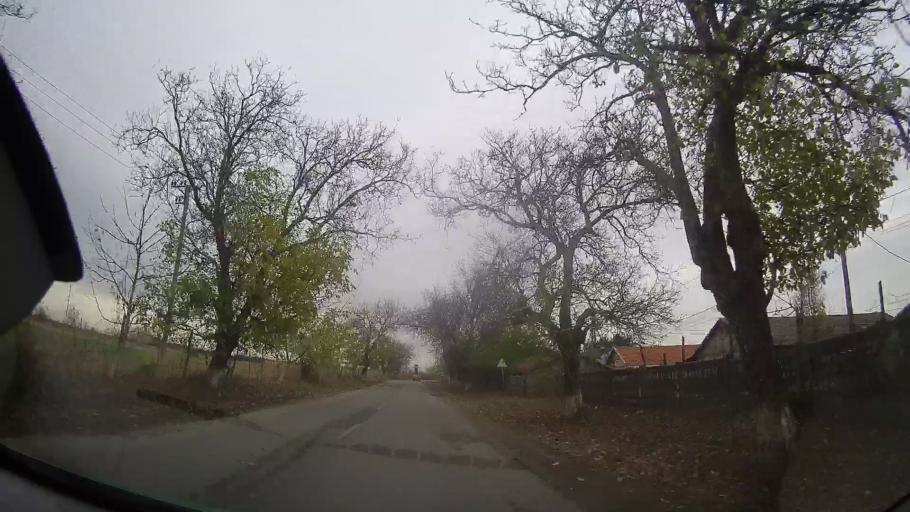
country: RO
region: Prahova
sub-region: Comuna Vadu Sapat
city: Vadu Sapat
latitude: 45.0278
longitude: 26.3914
